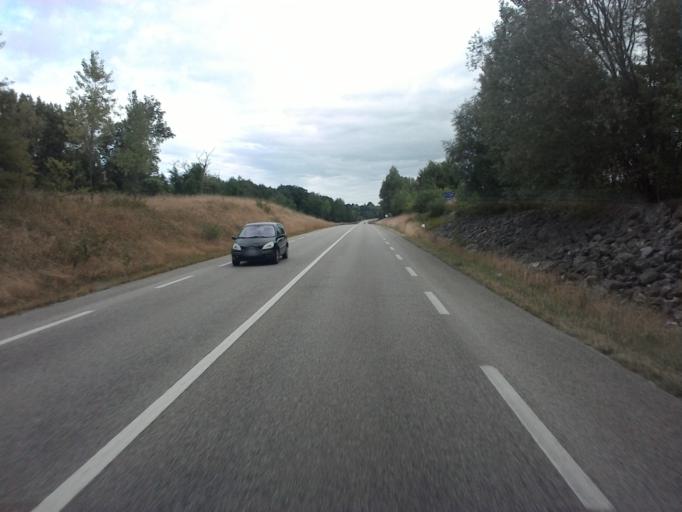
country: FR
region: Rhone-Alpes
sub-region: Departement de l'Ain
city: Lagnieu
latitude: 45.9012
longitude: 5.3372
